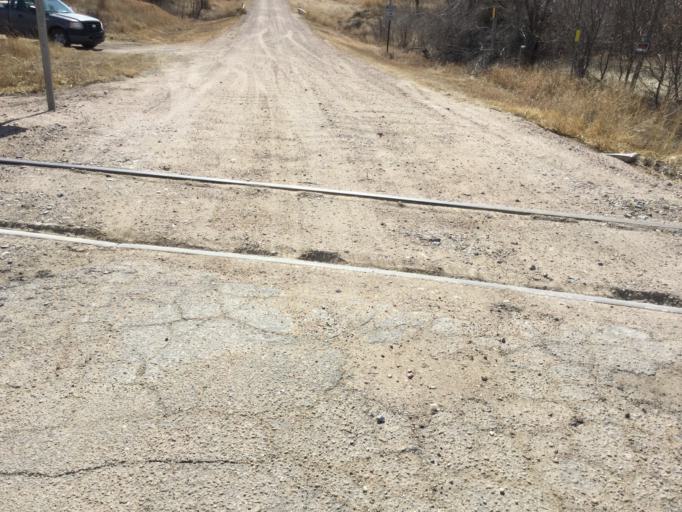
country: US
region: Kansas
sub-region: Pawnee County
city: Larned
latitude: 38.1896
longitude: -99.3505
